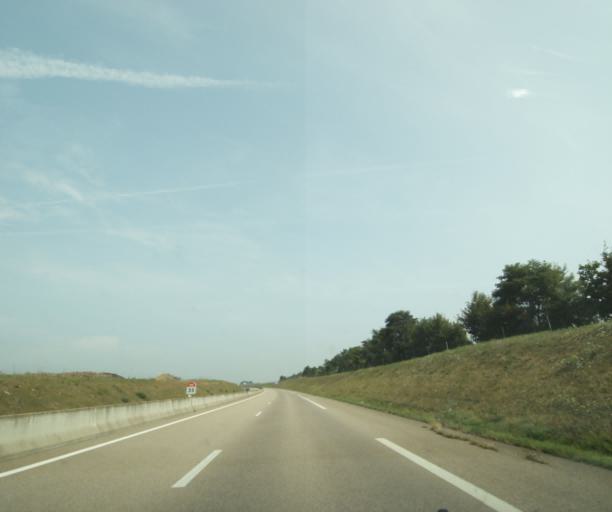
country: FR
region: Lower Normandy
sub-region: Departement de l'Orne
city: Courteilles
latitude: 48.8046
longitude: -0.1258
